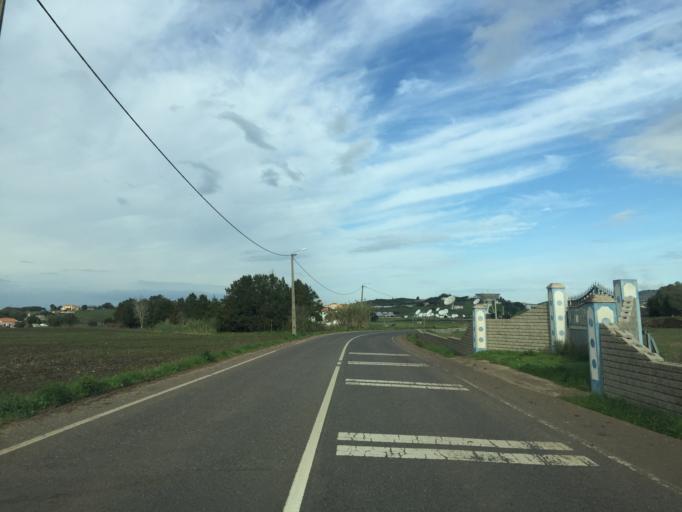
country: PT
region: Lisbon
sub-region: Sintra
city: Almargem
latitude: 38.8610
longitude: -9.2789
